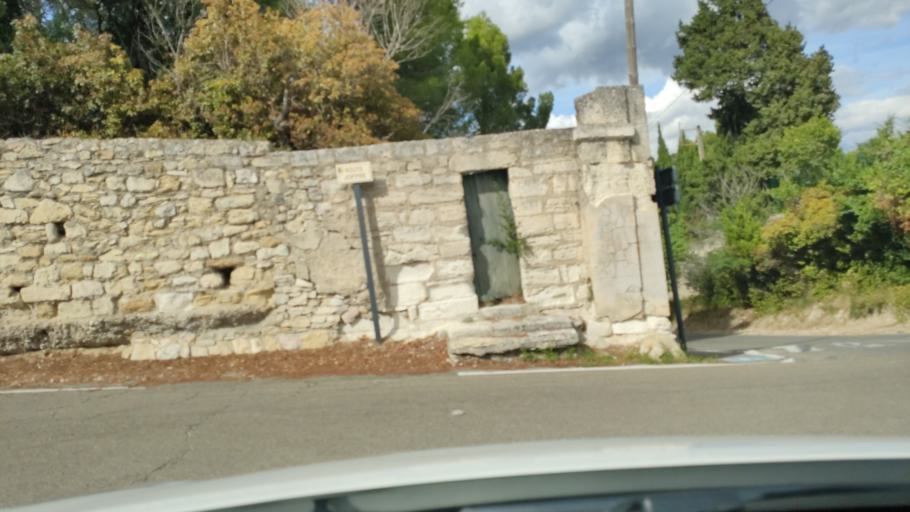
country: FR
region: Languedoc-Roussillon
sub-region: Departement du Gard
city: Villeneuve-les-Avignon
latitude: 43.9604
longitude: 4.7925
